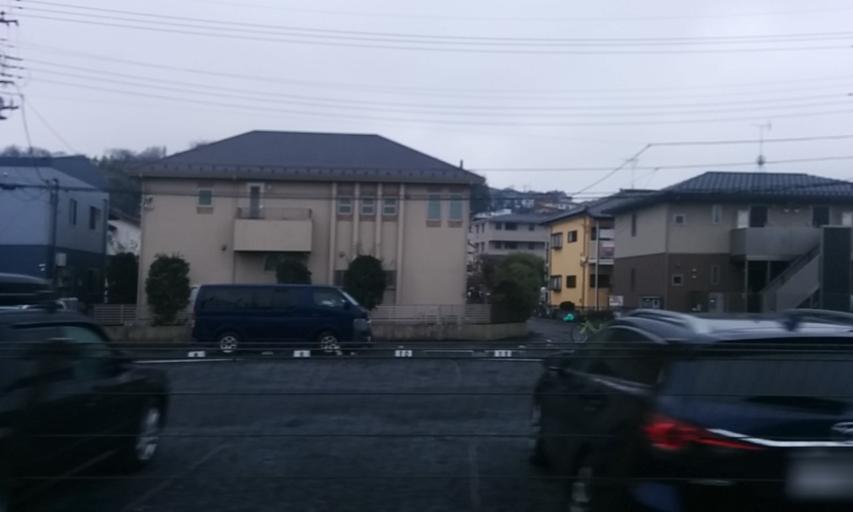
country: JP
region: Tokyo
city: Hino
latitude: 35.6603
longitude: 139.4193
